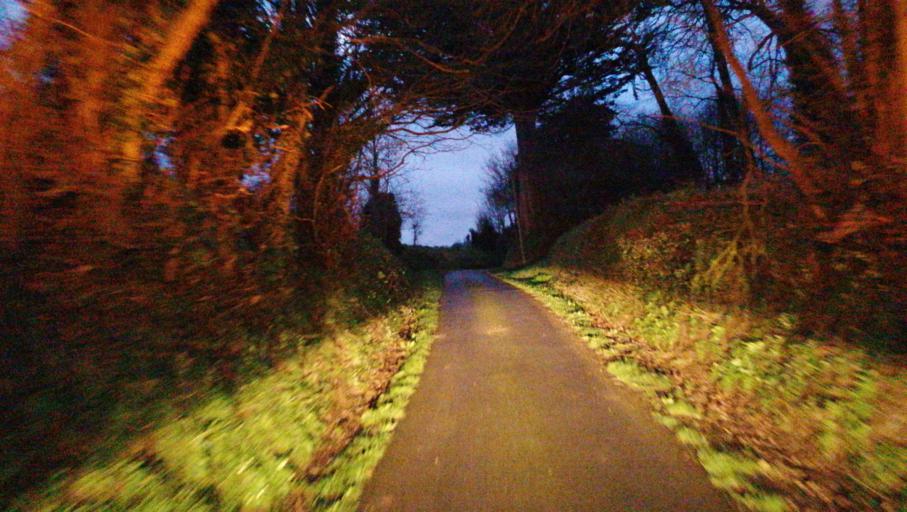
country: FR
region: Brittany
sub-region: Departement des Cotes-d'Armor
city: Plehedel
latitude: 48.6778
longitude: -3.0389
